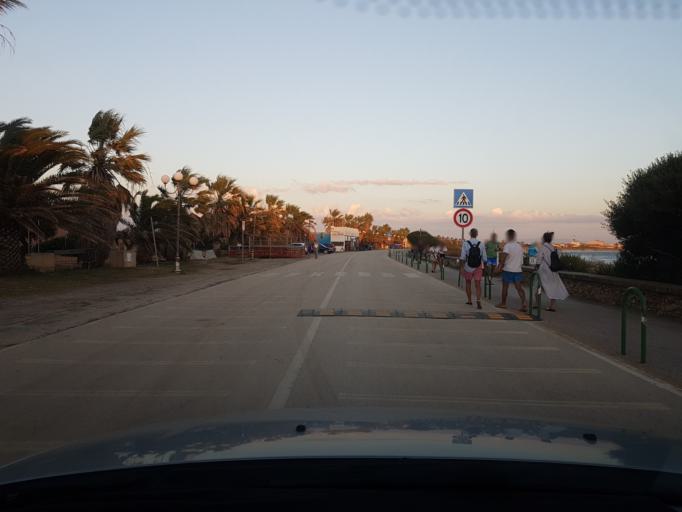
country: IT
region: Sardinia
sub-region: Provincia di Oristano
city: Riola Sardo
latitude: 40.0331
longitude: 8.4010
